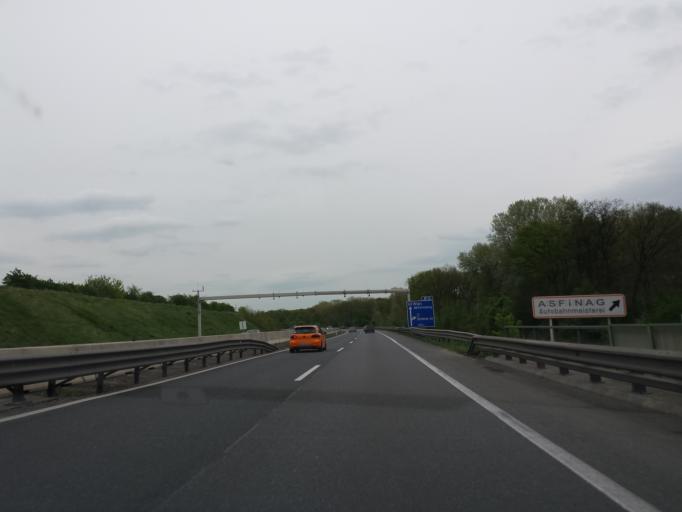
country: AT
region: Lower Austria
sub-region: Politischer Bezirk Korneuburg
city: Stockerau
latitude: 48.3782
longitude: 16.2228
